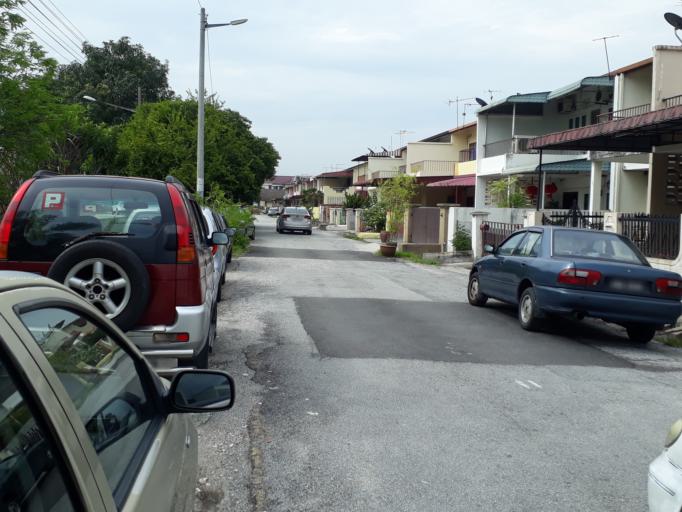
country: MY
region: Perak
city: Ipoh
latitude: 4.6115
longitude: 101.1088
